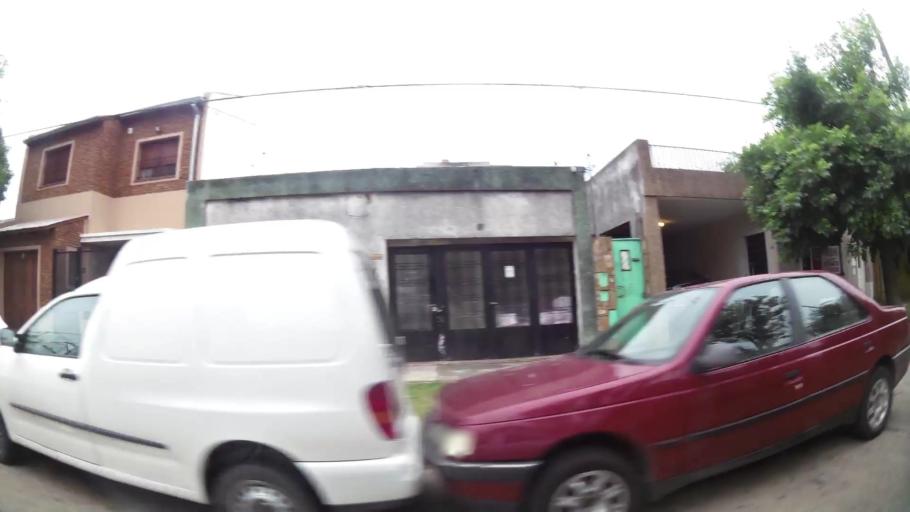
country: AR
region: Santa Fe
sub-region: Departamento de Rosario
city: Rosario
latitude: -32.9101
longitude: -60.6861
